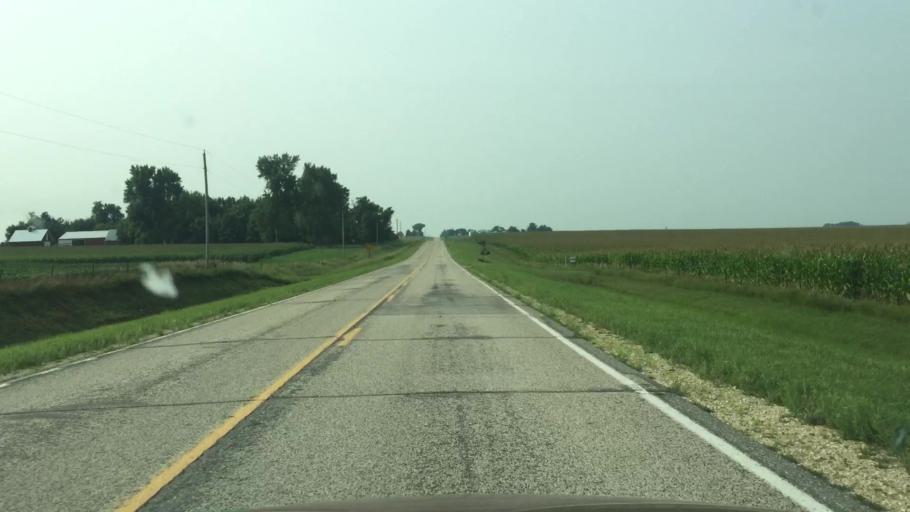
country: US
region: Iowa
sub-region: Osceola County
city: Sibley
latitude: 43.2802
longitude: -95.7829
